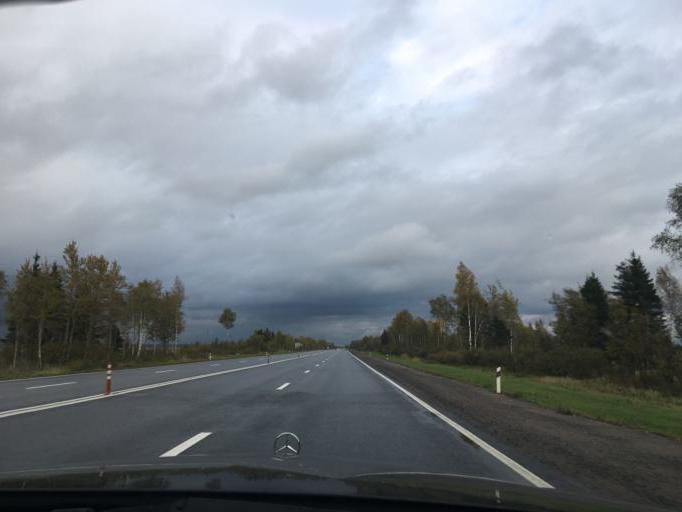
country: RU
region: Smolensk
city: Pechersk
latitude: 54.8532
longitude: 31.8669
